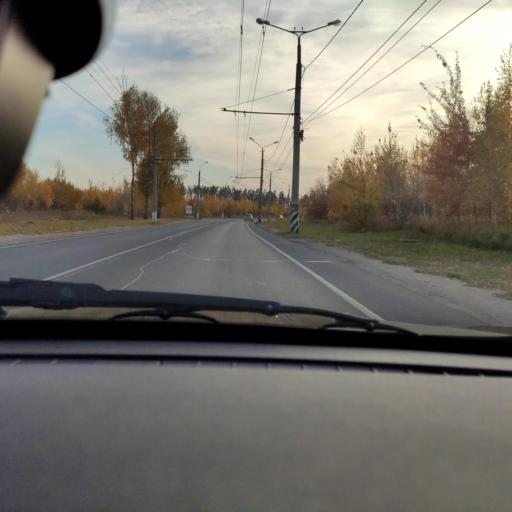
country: RU
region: Samara
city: Tol'yatti
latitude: 53.4840
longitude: 49.3799
